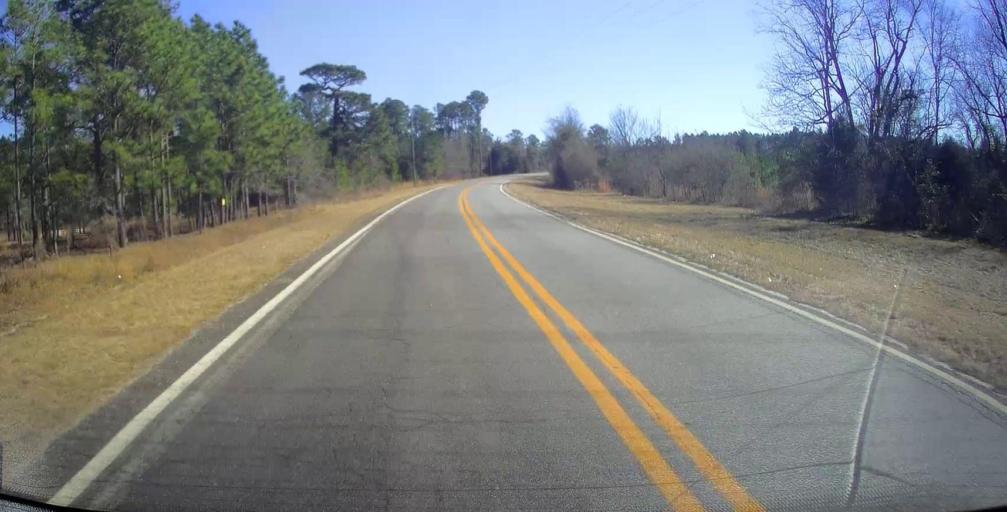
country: US
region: Georgia
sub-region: Crawford County
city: Roberta
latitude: 32.6307
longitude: -83.9911
